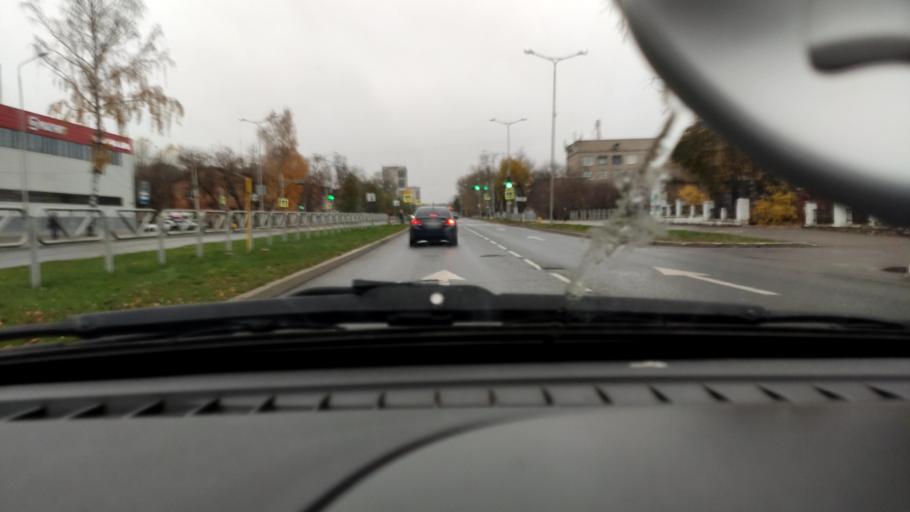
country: RU
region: Perm
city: Kultayevo
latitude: 58.0009
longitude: 55.9445
